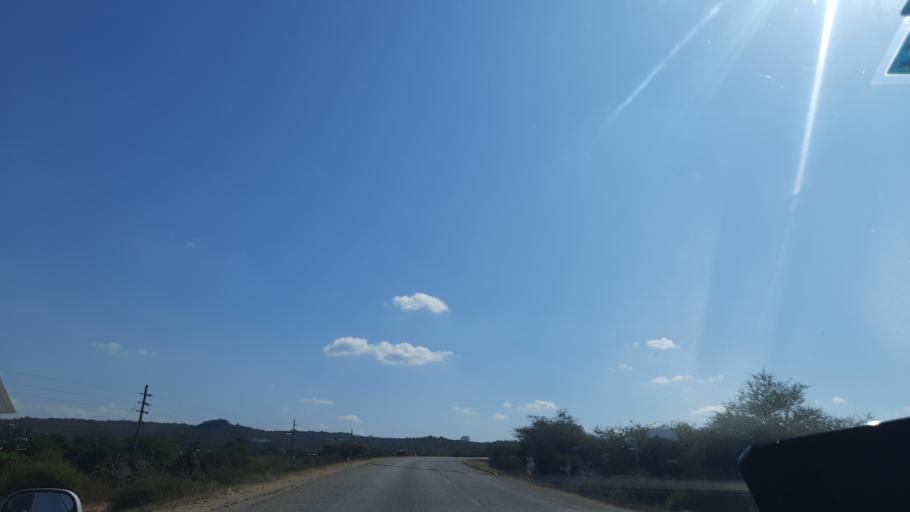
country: TZ
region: Singida
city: Kilimatinde
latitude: -5.7828
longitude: 34.8893
